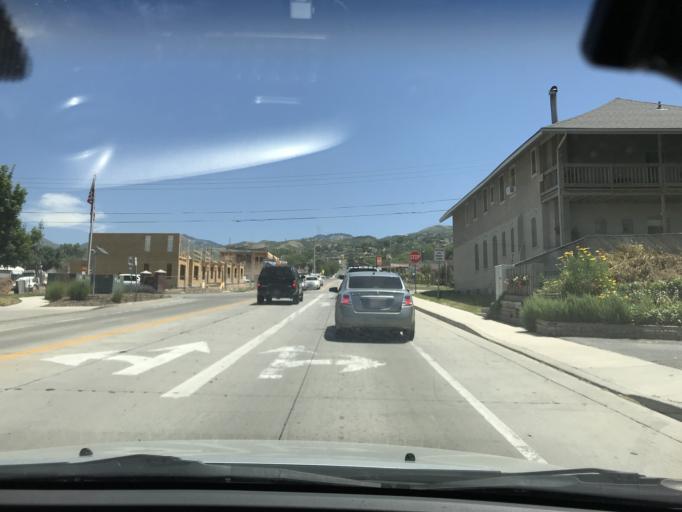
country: US
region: Utah
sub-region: Davis County
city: North Salt Lake
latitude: 40.8418
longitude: -111.9124
